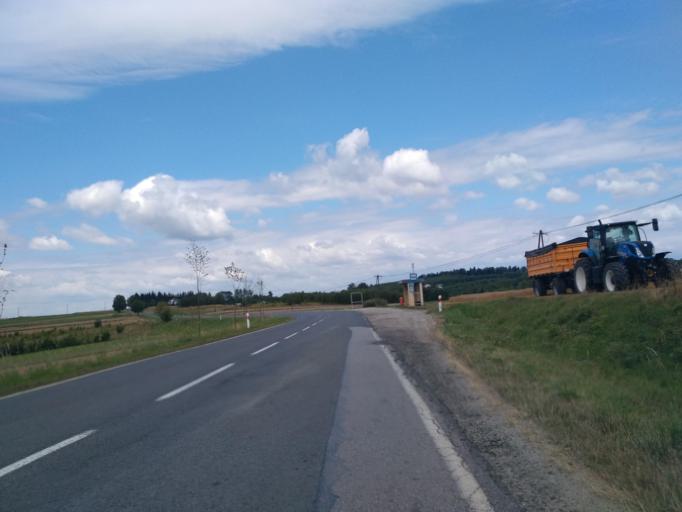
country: PL
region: Subcarpathian Voivodeship
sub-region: Powiat przeworski
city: Jawornik Polski
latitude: 49.8890
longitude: 22.2400
